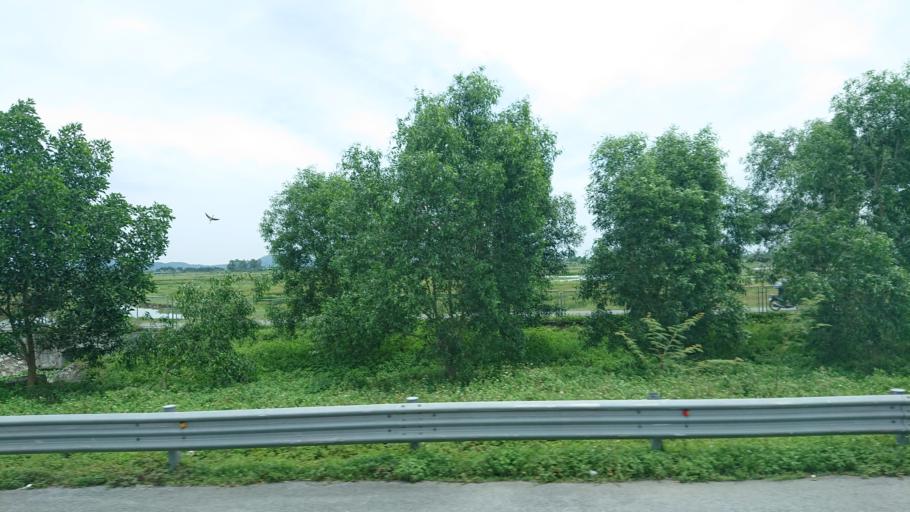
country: VN
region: Hai Phong
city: Nui Doi
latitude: 20.7658
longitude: 106.6542
